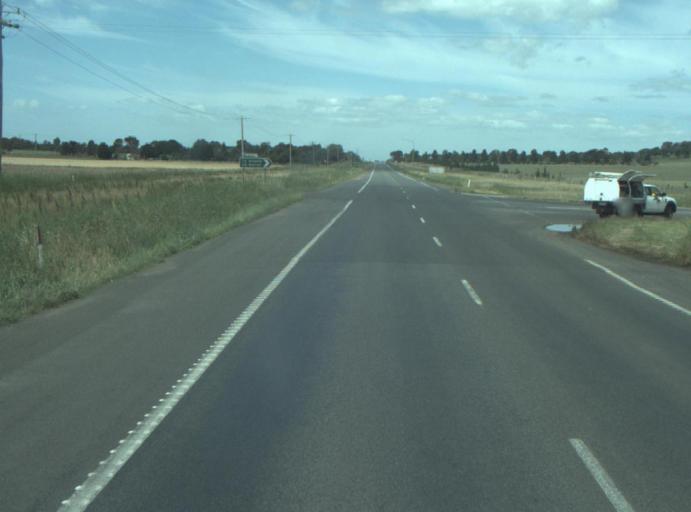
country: AU
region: Victoria
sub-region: Greater Geelong
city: Lara
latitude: -38.0141
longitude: 144.3514
